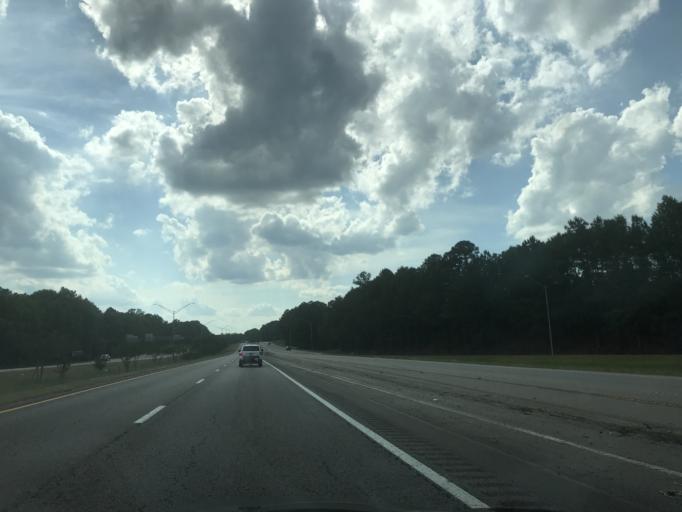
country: US
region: North Carolina
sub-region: Nash County
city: Red Oak
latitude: 35.9822
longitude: -77.8791
